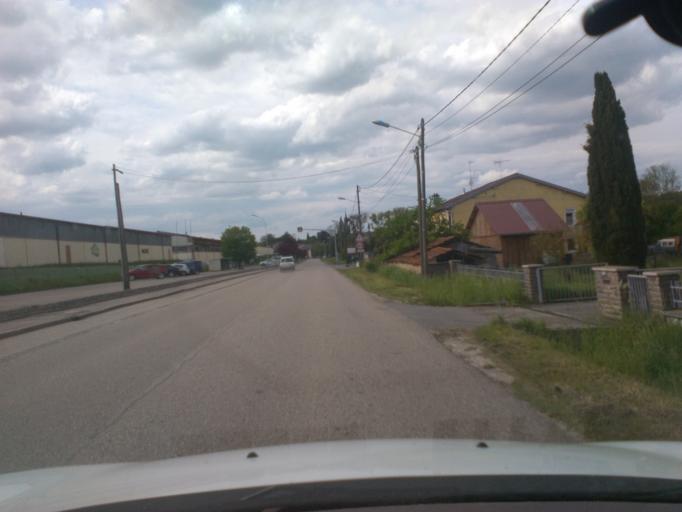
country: FR
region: Lorraine
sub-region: Departement des Vosges
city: Mirecourt
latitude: 48.2736
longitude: 6.1369
